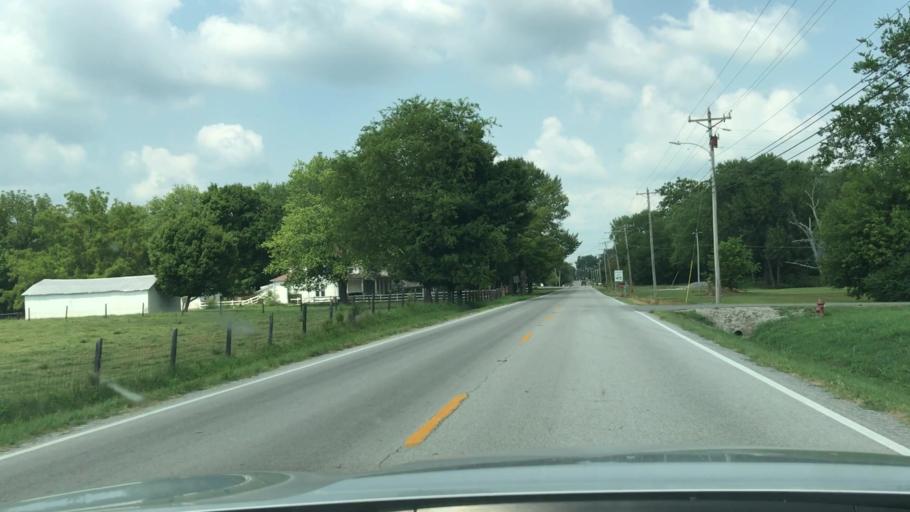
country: US
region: Kentucky
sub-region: Todd County
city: Elkton
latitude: 36.8074
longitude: -87.1403
